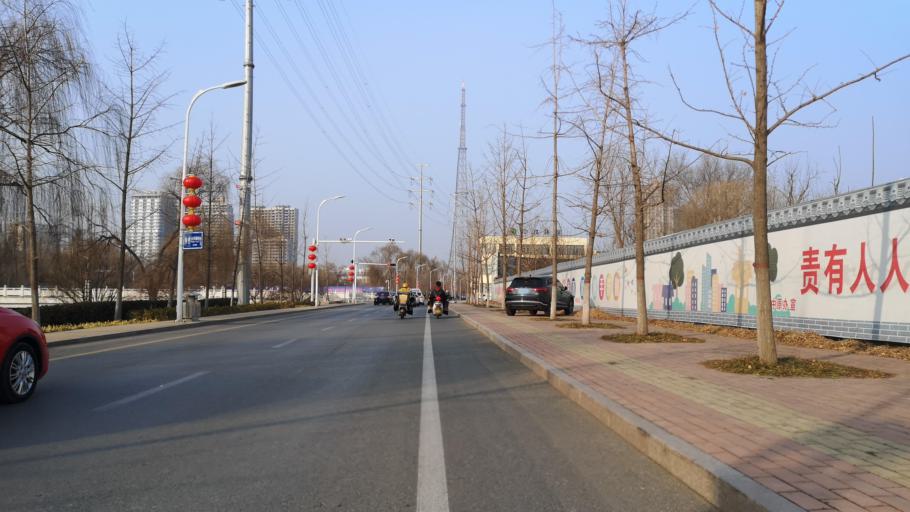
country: CN
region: Henan Sheng
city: Zhongyuanlu
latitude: 35.7748
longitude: 115.0486
